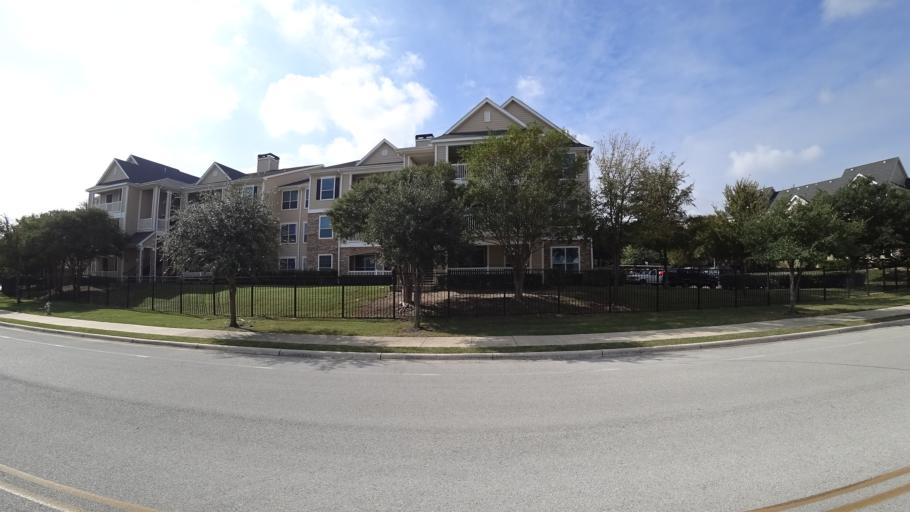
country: US
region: Texas
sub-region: Williamson County
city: Jollyville
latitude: 30.4371
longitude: -97.7312
